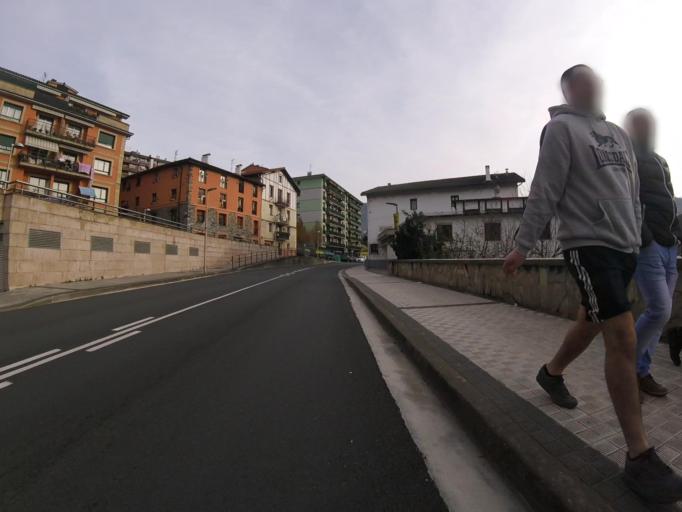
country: ES
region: Basque Country
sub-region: Provincia de Guipuzcoa
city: Ibarra
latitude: 43.1324
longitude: -2.0649
